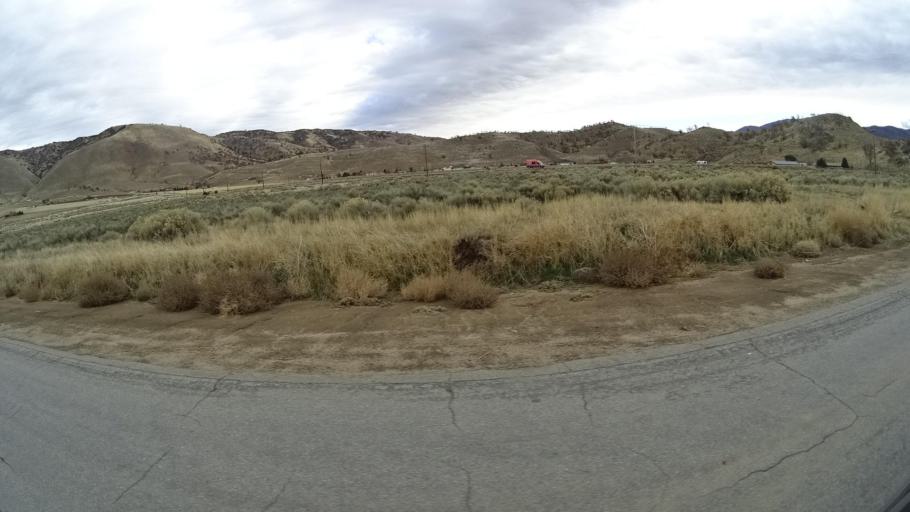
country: US
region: California
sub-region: Kern County
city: Bear Valley Springs
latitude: 35.1256
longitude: -118.5753
